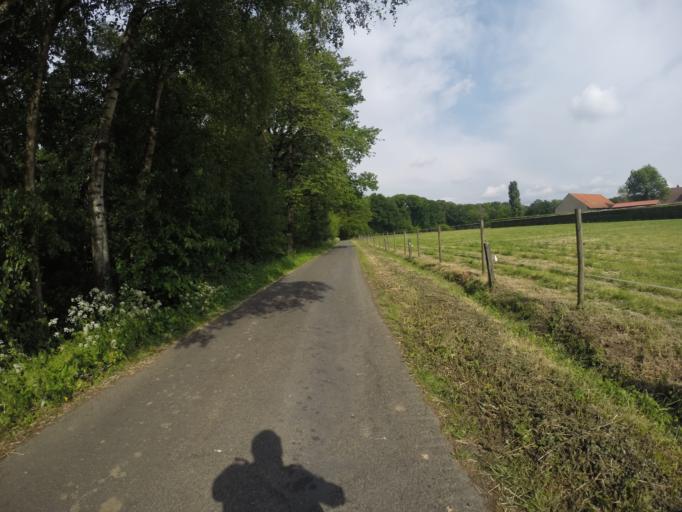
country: BE
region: Flanders
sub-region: Provincie West-Vlaanderen
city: Ruiselede
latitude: 51.0729
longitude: 3.3777
